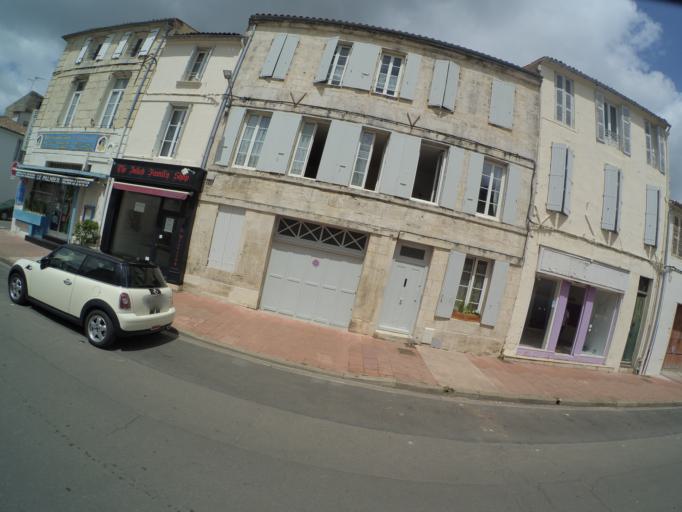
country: FR
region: Poitou-Charentes
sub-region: Departement de la Charente-Maritime
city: Rochefort
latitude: 45.9341
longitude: -0.9605
